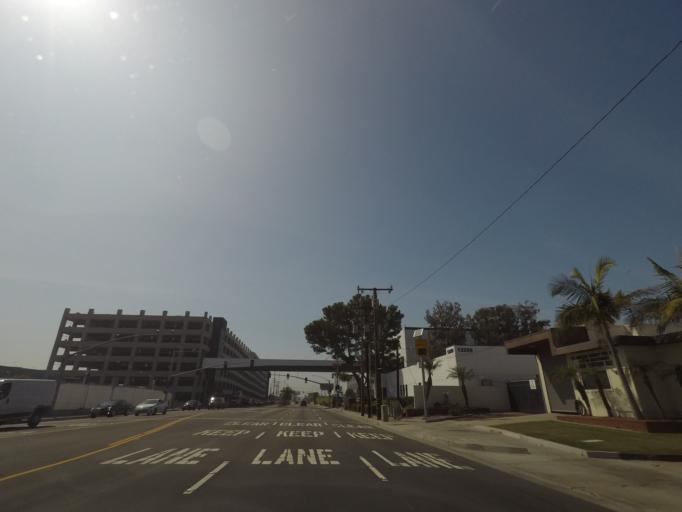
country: US
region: California
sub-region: Los Angeles County
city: West Athens
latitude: 33.9221
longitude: -118.3266
